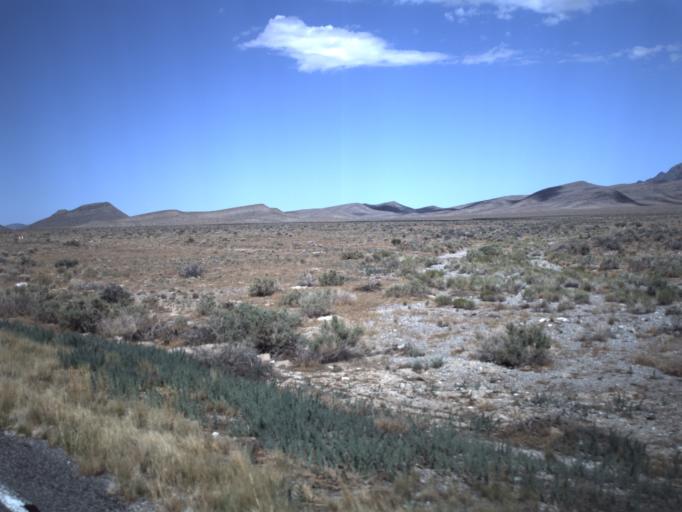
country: US
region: Utah
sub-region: Beaver County
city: Milford
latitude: 39.0377
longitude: -113.3212
